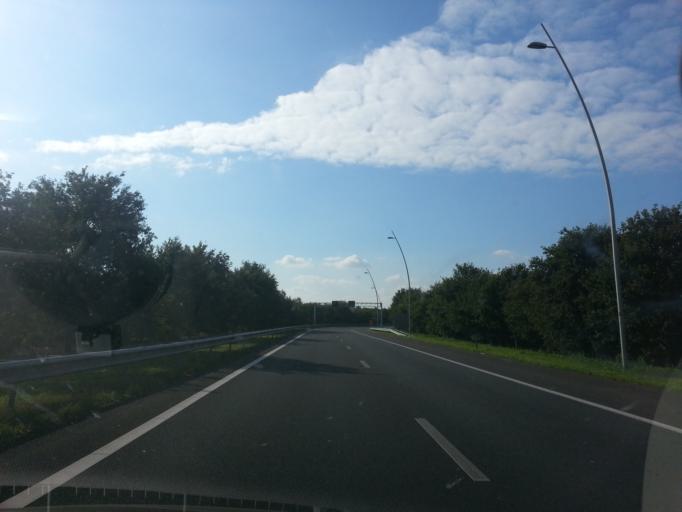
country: NL
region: North Brabant
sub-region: Gemeente Best
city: Best
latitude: 51.4930
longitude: 5.4365
